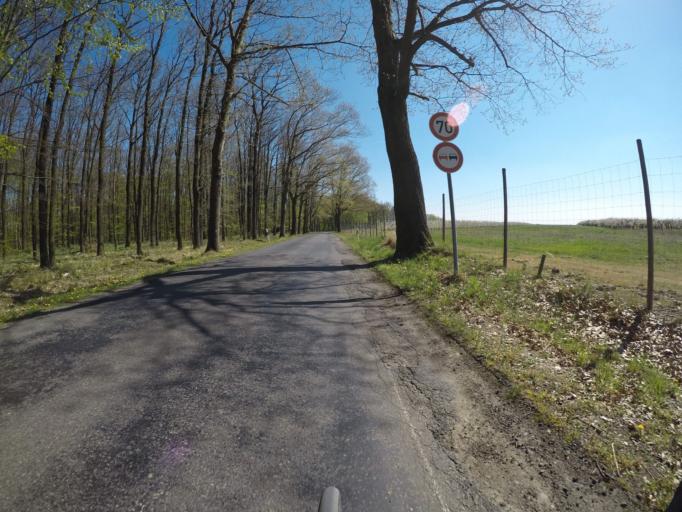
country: DE
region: Brandenburg
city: Werftpfuhl
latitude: 52.6239
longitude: 13.8212
